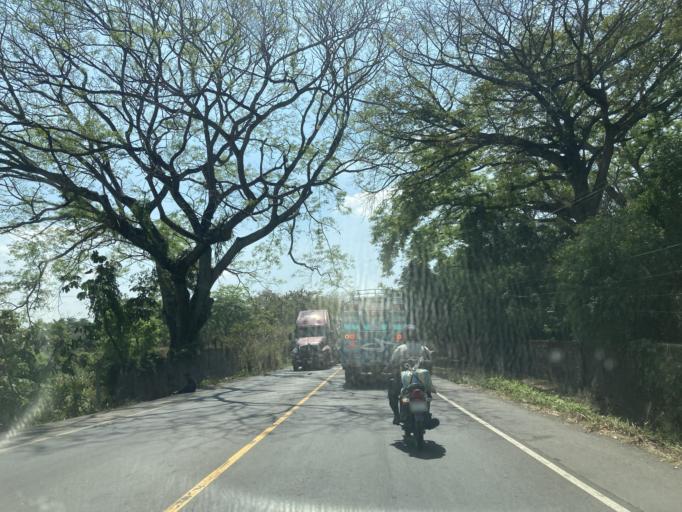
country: GT
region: Escuintla
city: Guanagazapa
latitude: 14.2169
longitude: -90.7253
